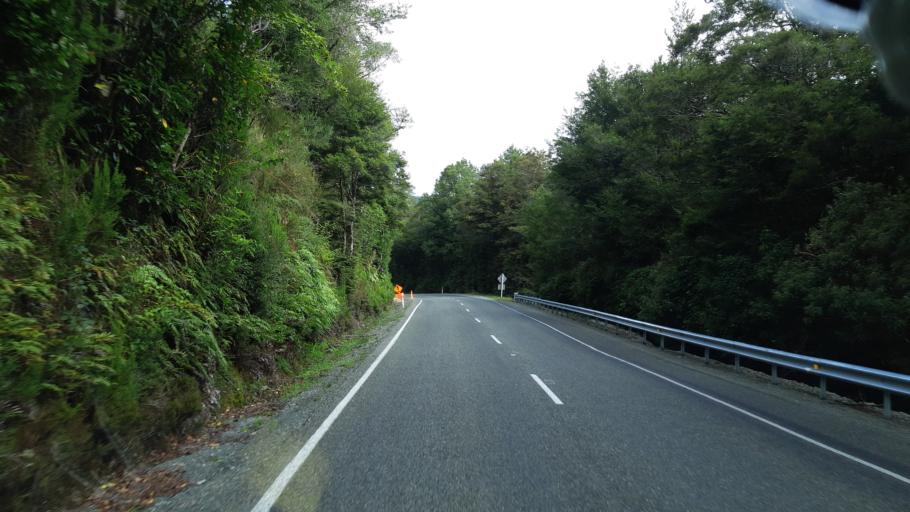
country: NZ
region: West Coast
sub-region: Buller District
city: Westport
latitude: -41.9856
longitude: 172.2088
